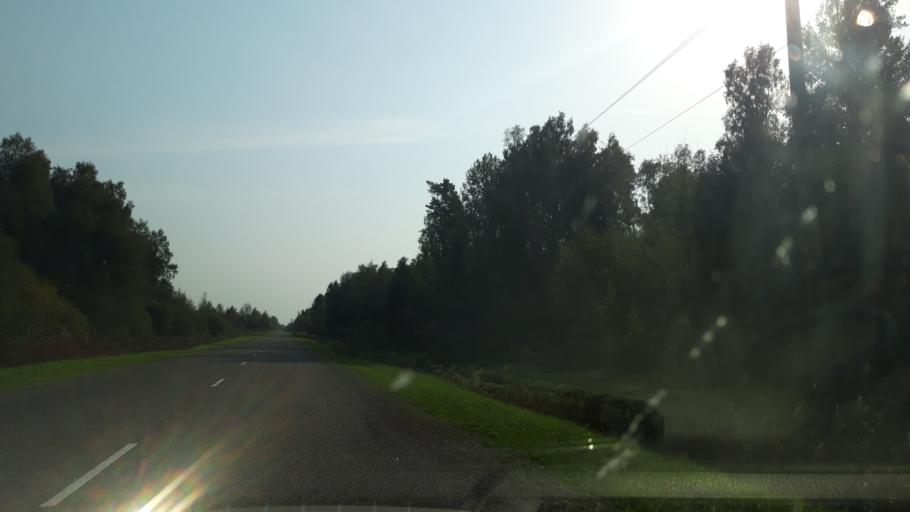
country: LV
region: Burtnieki
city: Matisi
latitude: 57.6429
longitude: 25.2467
